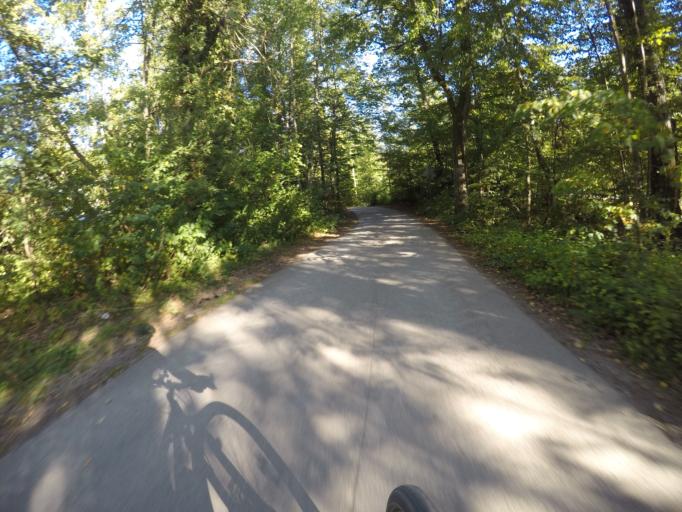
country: DE
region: Baden-Wuerttemberg
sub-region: Regierungsbezirk Stuttgart
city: Nufringen
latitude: 48.6027
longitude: 8.9023
